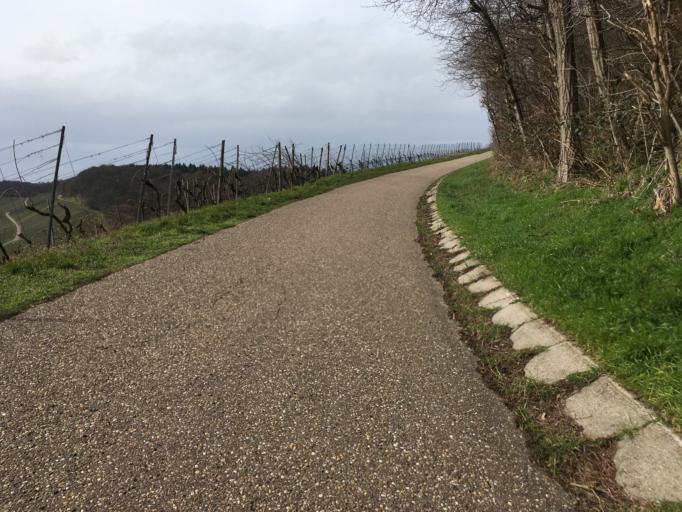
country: DE
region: Baden-Wuerttemberg
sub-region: Regierungsbezirk Stuttgart
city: Leingarten
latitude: 49.1231
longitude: 9.0974
